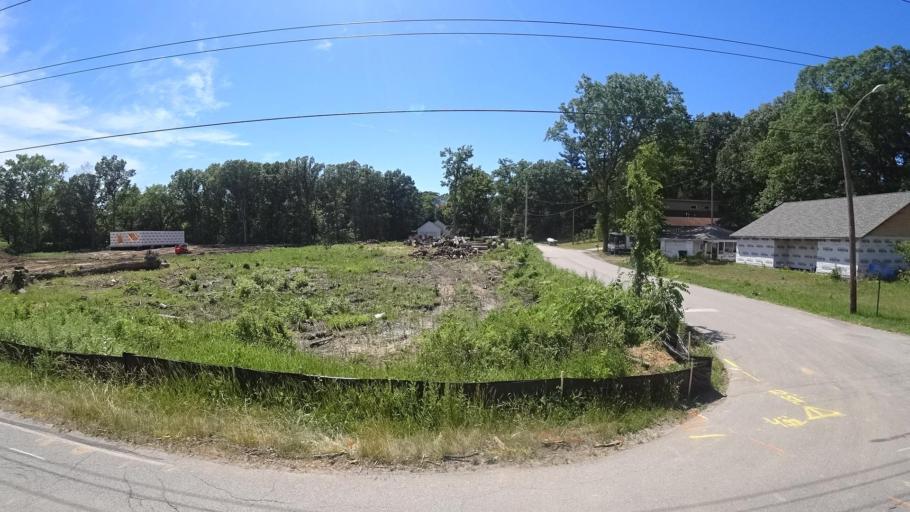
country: US
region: Indiana
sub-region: Porter County
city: Porter
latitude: 41.6378
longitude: -87.0673
